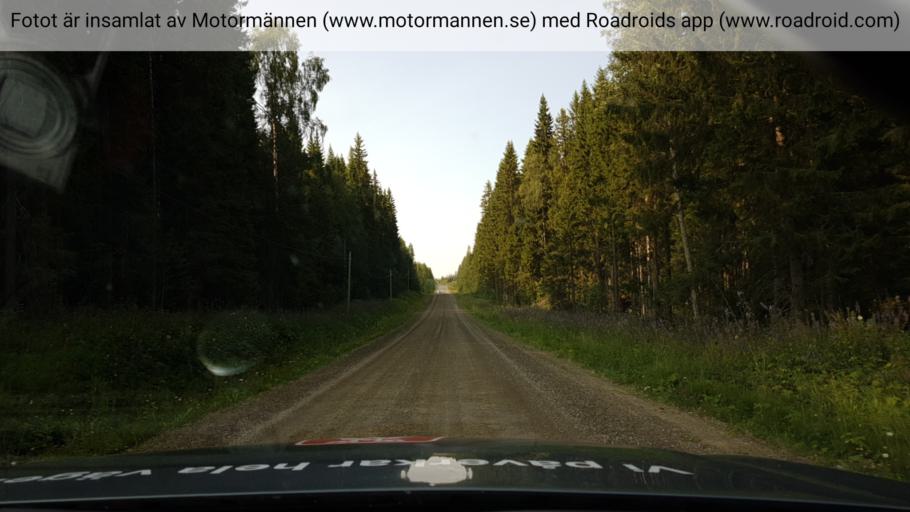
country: SE
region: Jaemtland
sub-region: OEstersunds Kommun
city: Brunflo
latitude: 62.6251
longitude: 14.9430
